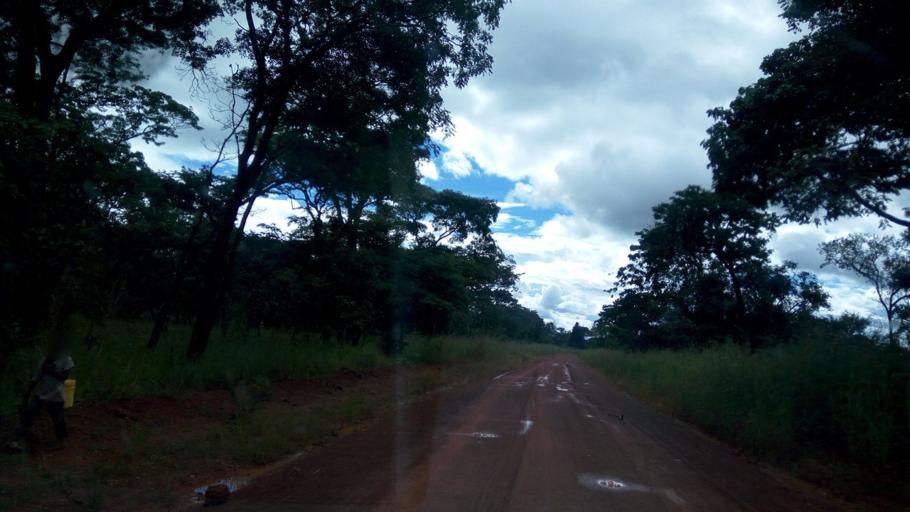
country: ZM
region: Luapula
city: Mwense
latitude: -10.7091
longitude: 28.1788
